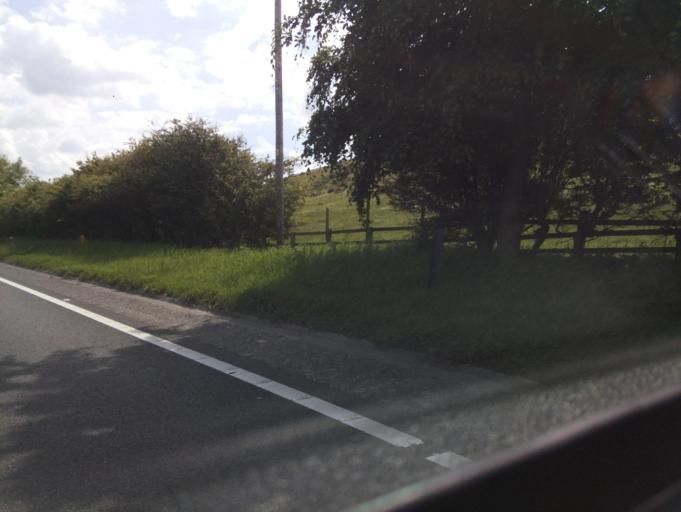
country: GB
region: England
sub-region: County Durham
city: Peterlee
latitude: 54.7148
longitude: -1.3245
